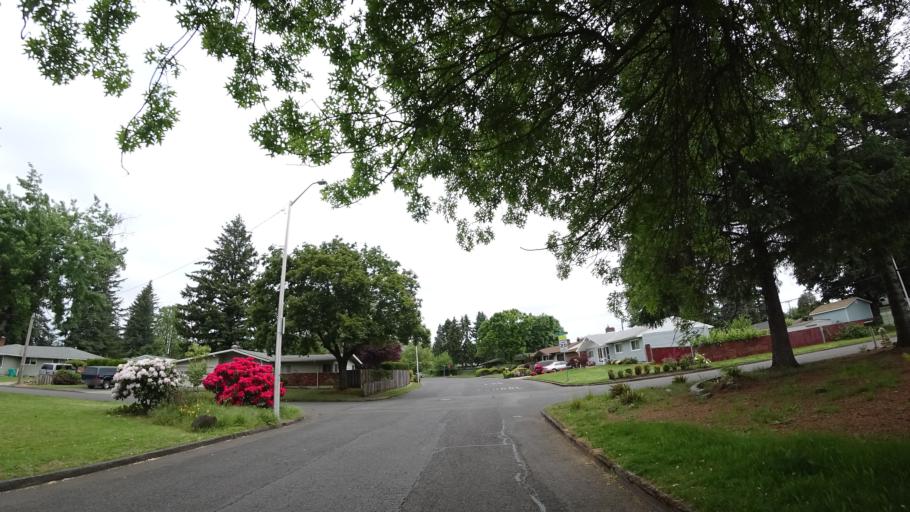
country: US
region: Oregon
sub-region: Multnomah County
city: Gresham
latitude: 45.5003
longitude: -122.4817
